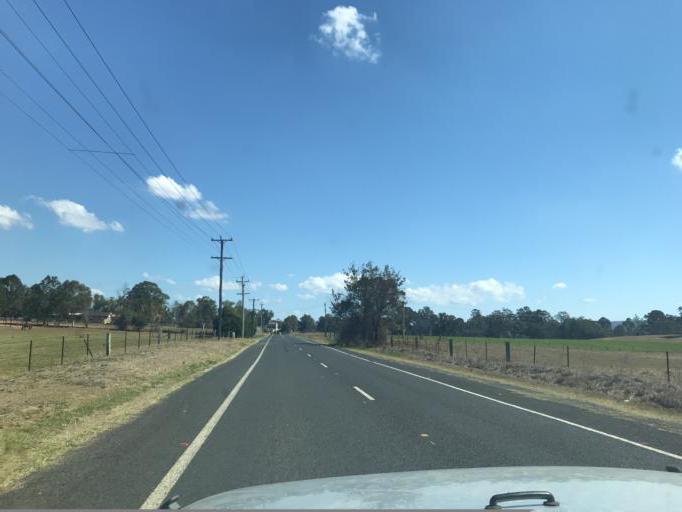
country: AU
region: New South Wales
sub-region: Hawkesbury
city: Richmond
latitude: -33.5738
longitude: 150.7296
